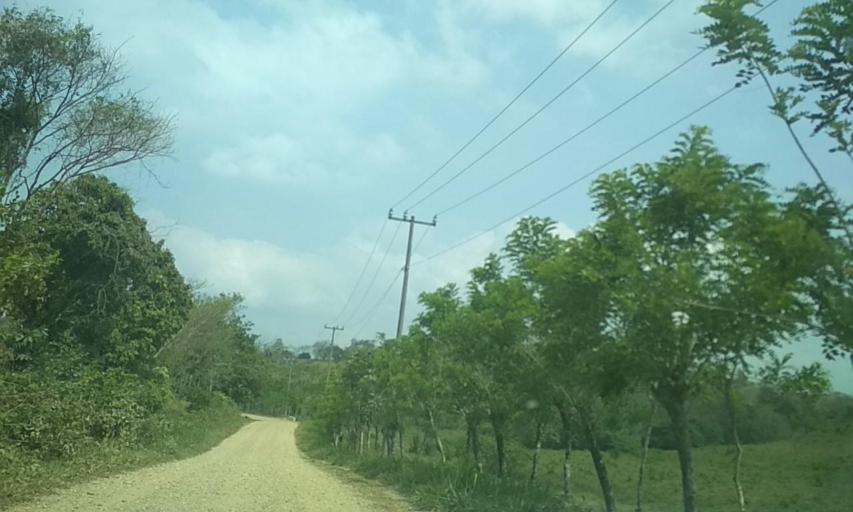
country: MX
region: Tabasco
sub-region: Huimanguillo
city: Francisco Rueda
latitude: 17.6502
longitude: -93.8077
